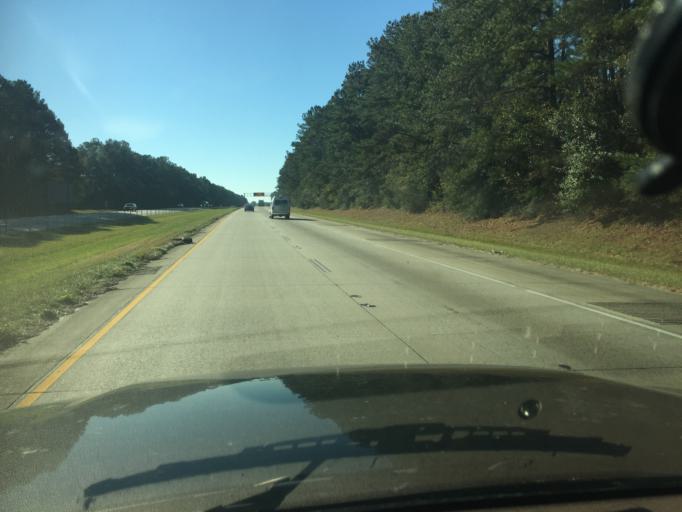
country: US
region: Louisiana
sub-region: Saint Tammany Parish
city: Pearl River
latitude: 30.3363
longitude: -89.7379
